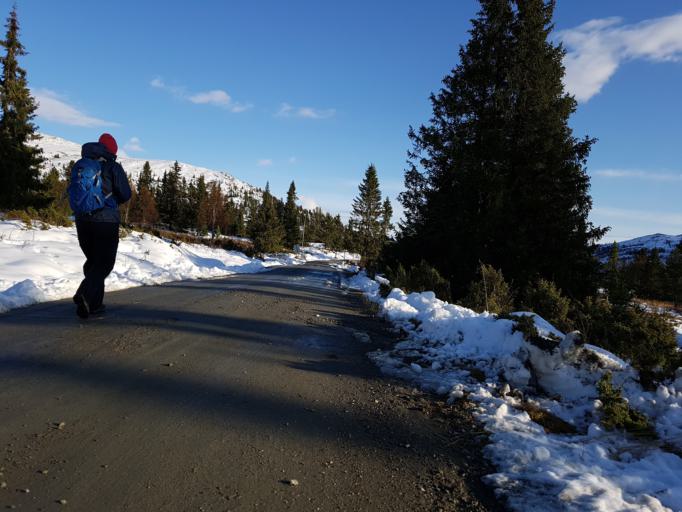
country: NO
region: Oppland
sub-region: Sel
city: Otta
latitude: 61.8129
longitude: 9.6829
